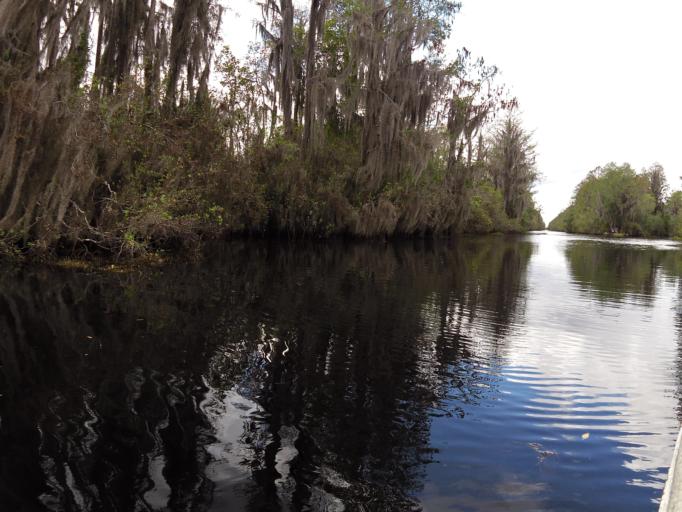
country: US
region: Georgia
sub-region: Charlton County
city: Folkston
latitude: 30.7374
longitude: -82.1706
